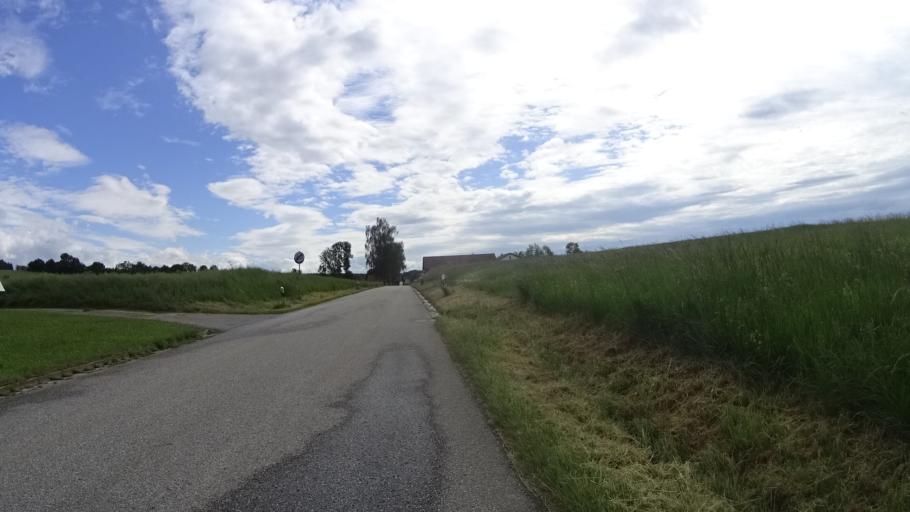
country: DE
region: Bavaria
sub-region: Lower Bavaria
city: Furth
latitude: 48.4019
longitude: 12.3652
